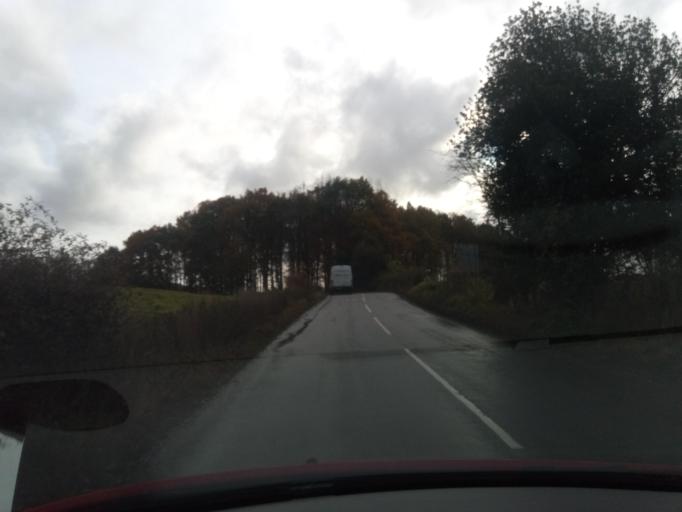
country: GB
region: England
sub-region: Northumberland
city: Birtley
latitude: 55.0579
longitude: -2.1924
